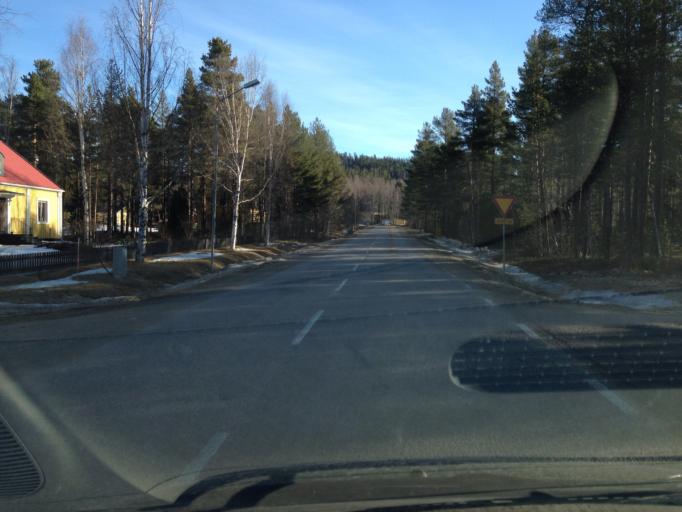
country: SE
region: Jaemtland
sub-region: Harjedalens Kommun
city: Sveg
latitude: 62.1553
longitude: 13.8875
